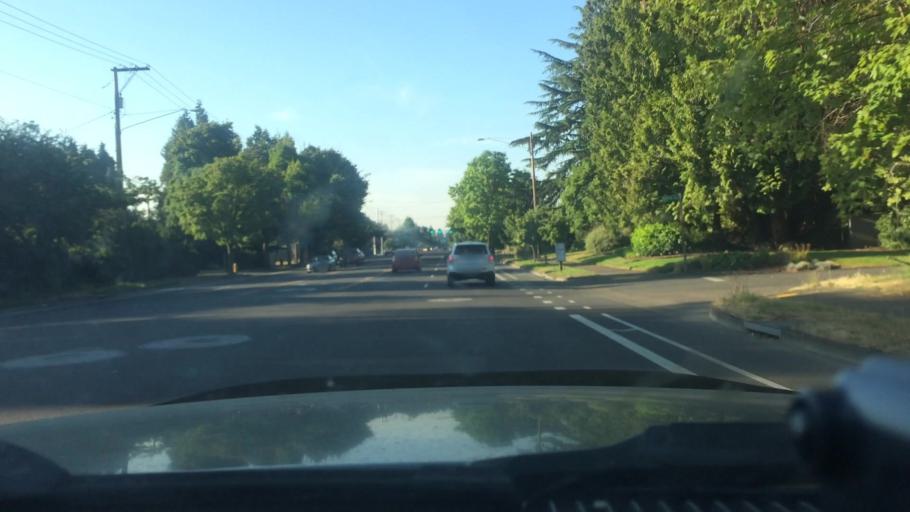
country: US
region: Oregon
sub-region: Lane County
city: Eugene
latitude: 44.0837
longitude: -123.1232
